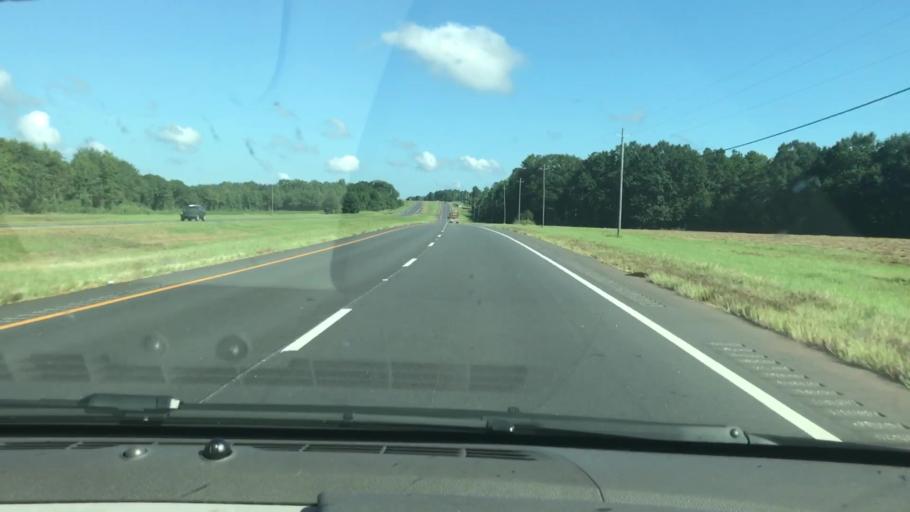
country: US
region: Alabama
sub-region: Barbour County
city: Eufaula
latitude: 32.0197
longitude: -85.1177
